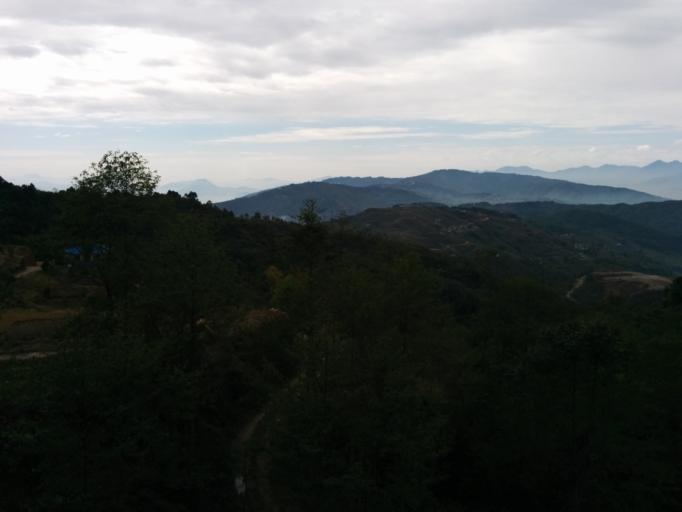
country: NP
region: Central Region
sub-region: Bagmati Zone
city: Nagarkot
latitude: 27.7746
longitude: 85.4918
